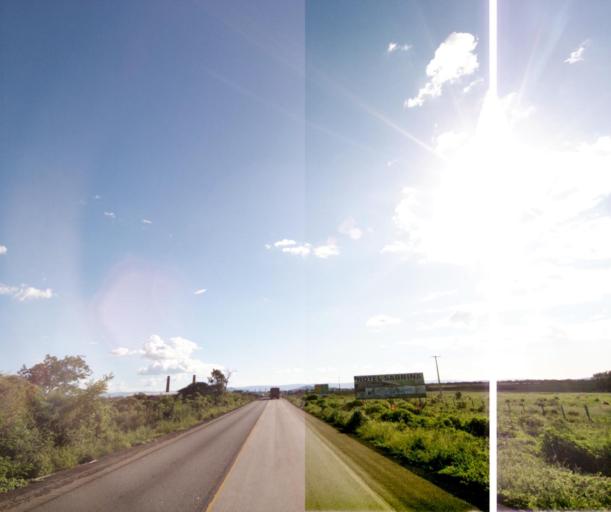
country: BR
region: Bahia
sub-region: Guanambi
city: Guanambi
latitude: -14.1801
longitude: -42.7338
